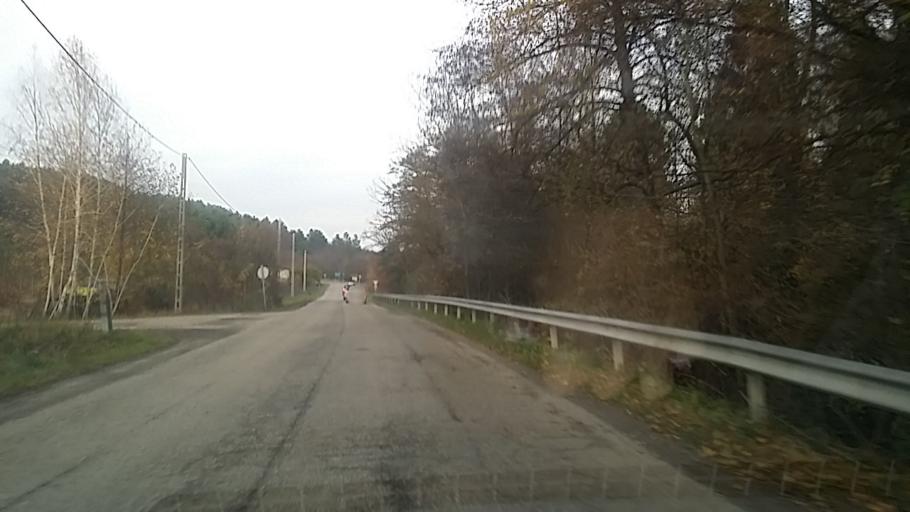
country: HU
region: Borsod-Abauj-Zemplen
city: Sarospatak
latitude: 48.4681
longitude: 21.4980
